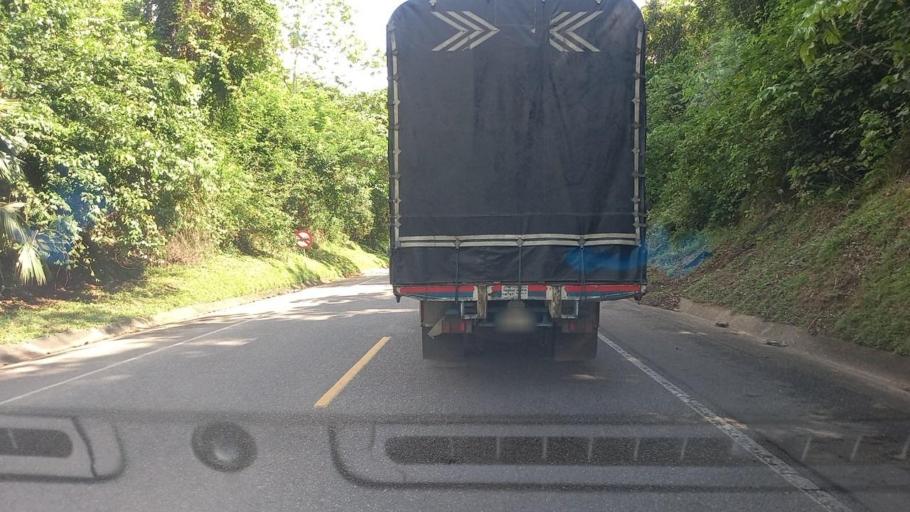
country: CO
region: Santander
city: Barrancabermeja
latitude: 6.9747
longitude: -73.6992
